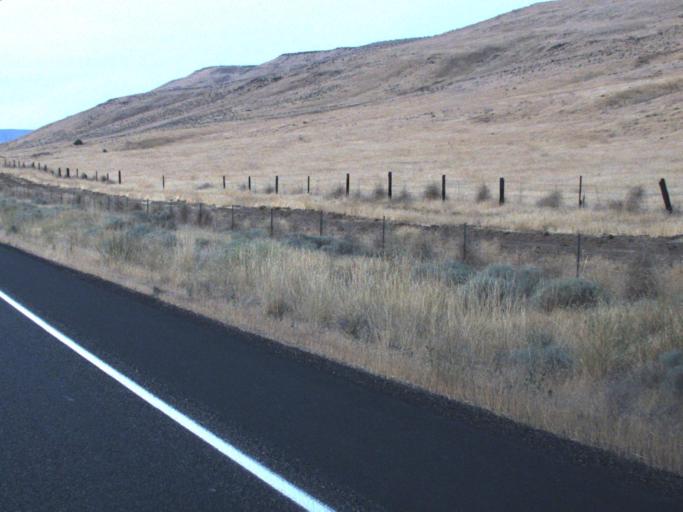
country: US
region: Washington
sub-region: Yakima County
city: Toppenish
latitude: 46.1683
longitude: -120.5052
